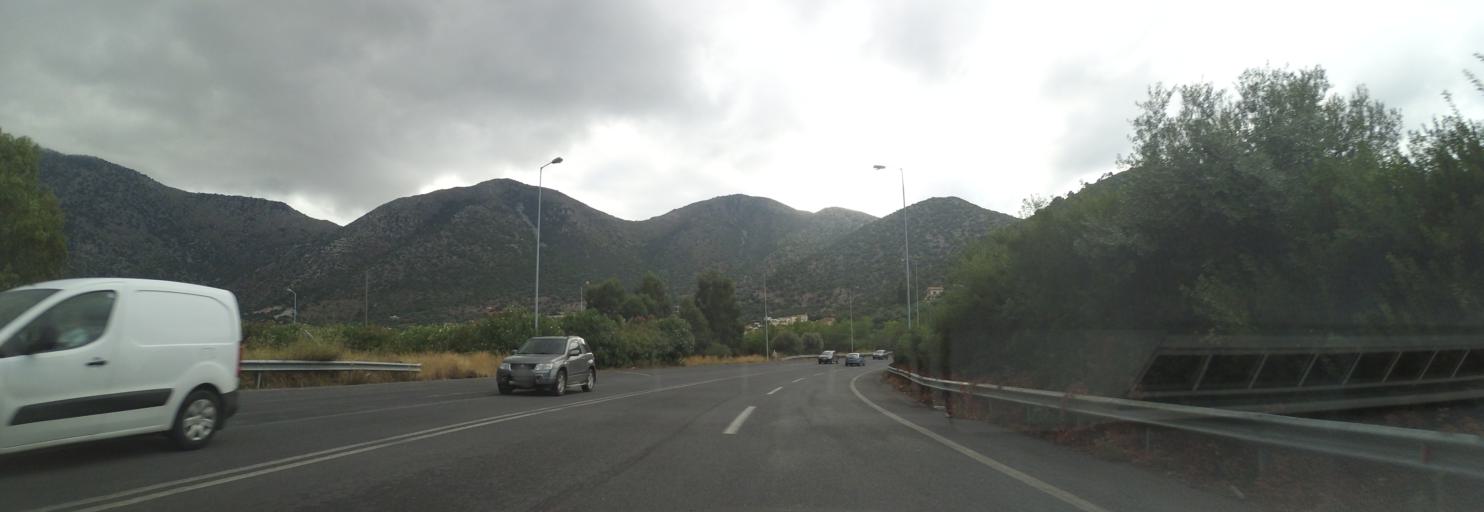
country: GR
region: Crete
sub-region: Nomos Rethymnis
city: Perama
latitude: 35.4018
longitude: 24.7862
